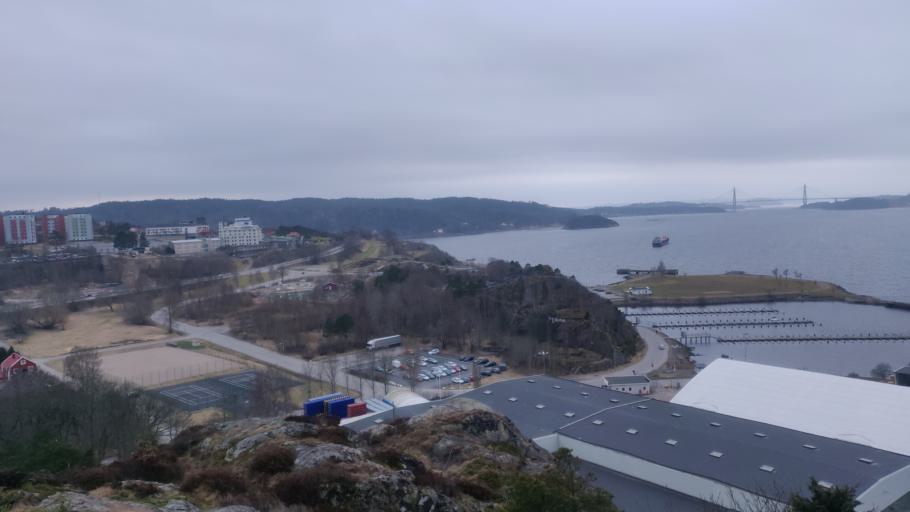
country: SE
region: Vaestra Goetaland
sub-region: Uddevalla Kommun
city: Uddevalla
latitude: 58.3440
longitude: 11.9142
